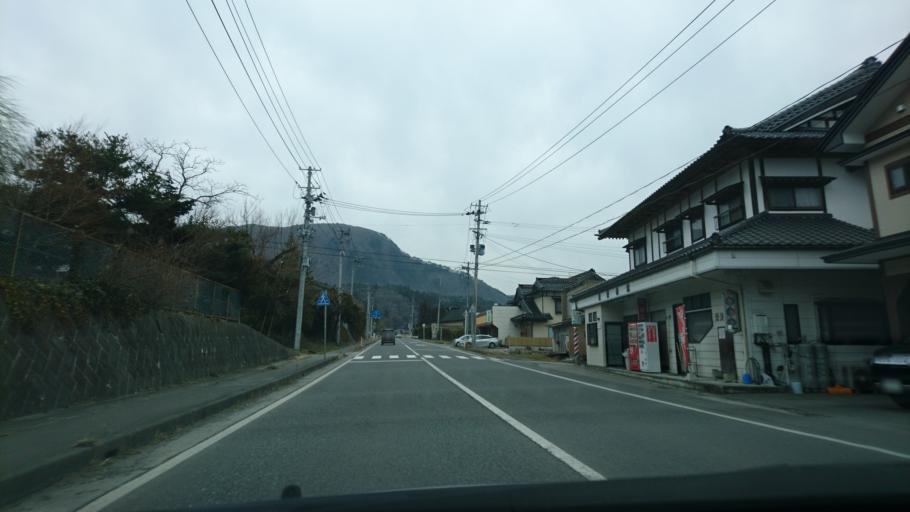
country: JP
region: Iwate
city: Tono
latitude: 39.1907
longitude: 141.5634
